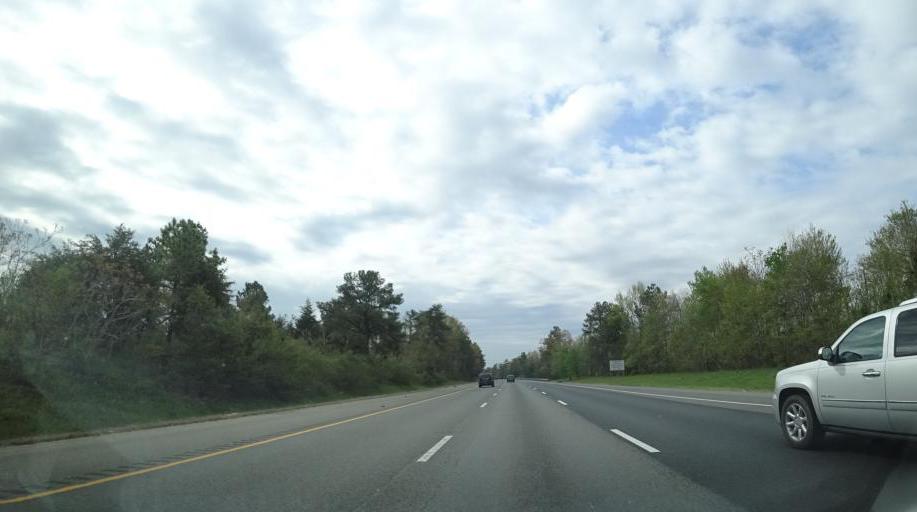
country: US
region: Virginia
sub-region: Caroline County
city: Bowling Green
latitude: 38.0141
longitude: -77.4993
